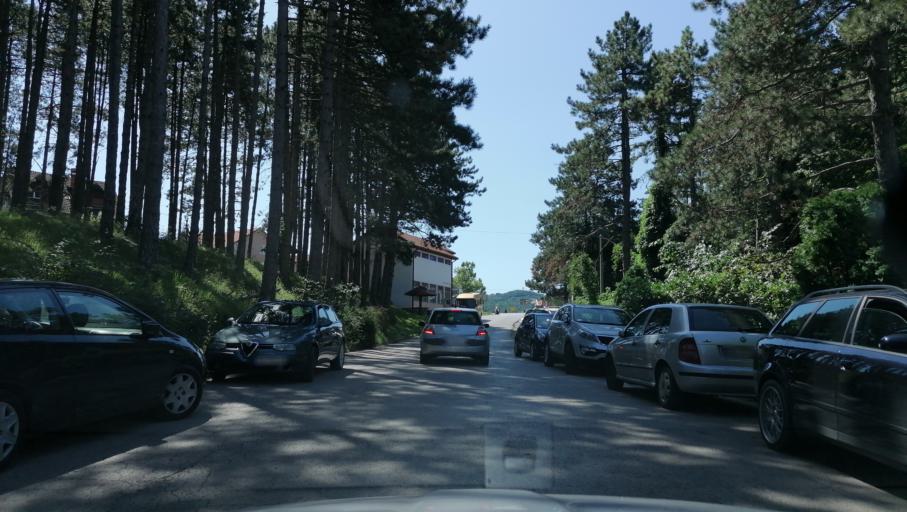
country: RS
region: Central Serbia
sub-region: Kolubarski Okrug
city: Valjevo
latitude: 44.2611
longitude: 19.8786
